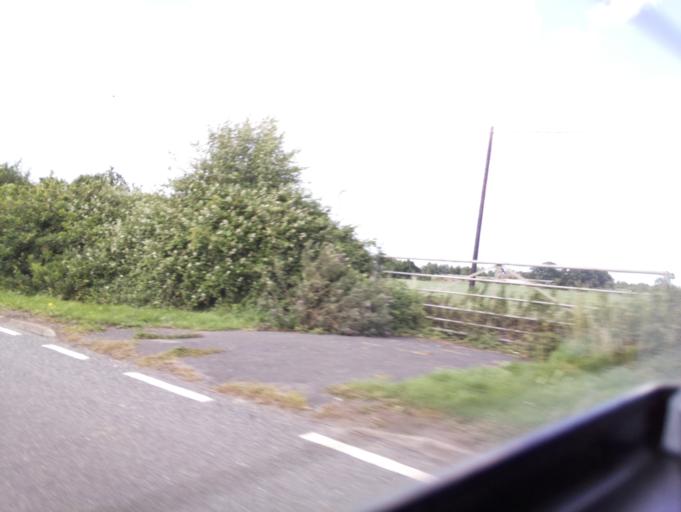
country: GB
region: England
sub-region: Leicestershire
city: Measham
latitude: 52.6748
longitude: -1.5424
